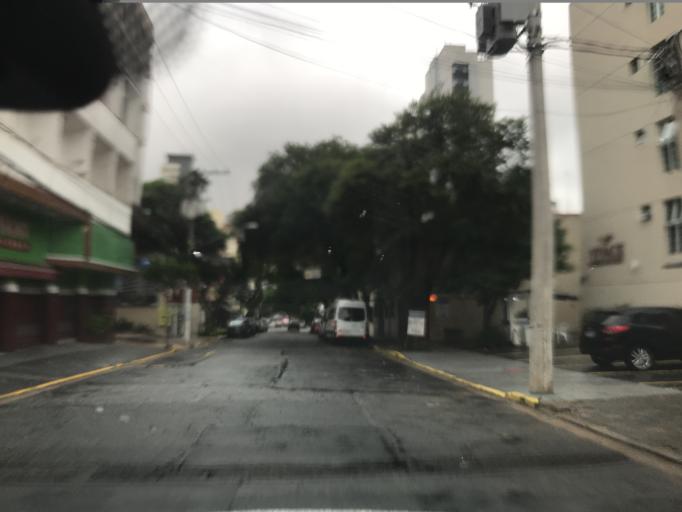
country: BR
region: Sao Paulo
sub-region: Sao Paulo
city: Sao Paulo
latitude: -23.5324
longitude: -46.6811
